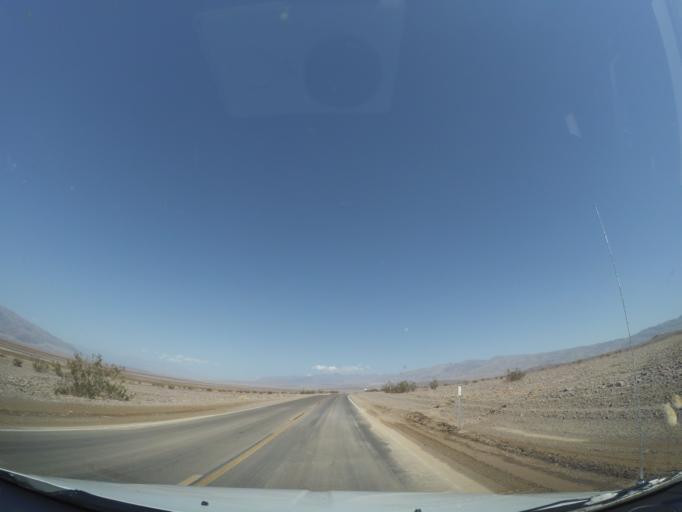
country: US
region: Nevada
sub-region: Nye County
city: Beatty
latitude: 36.5112
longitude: -116.8808
